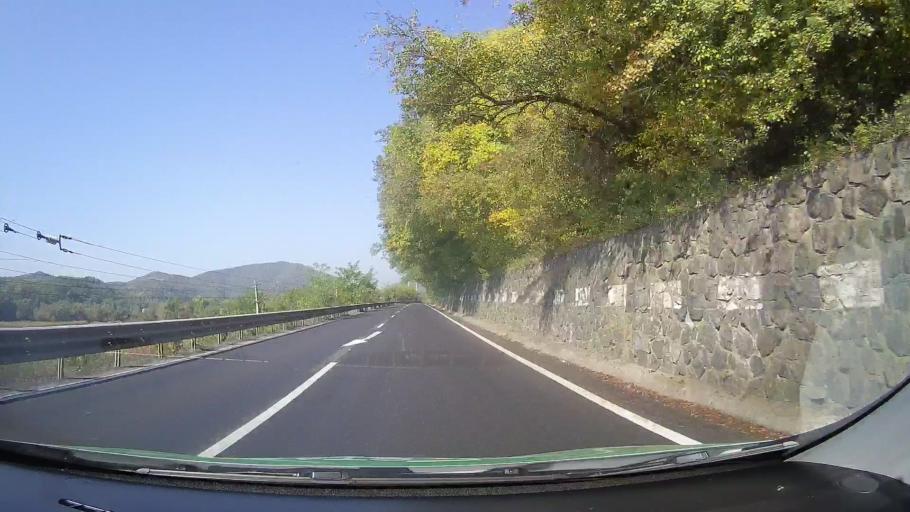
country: RO
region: Hunedoara
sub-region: Comuna Burjuc
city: Burjuc
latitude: 45.9444
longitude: 22.4968
